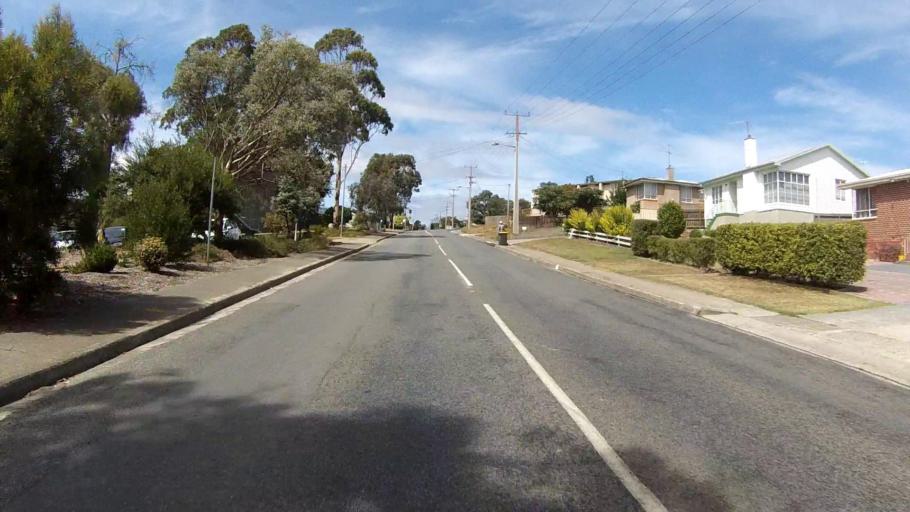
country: AU
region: Tasmania
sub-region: Clarence
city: Lindisfarne
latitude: -42.8110
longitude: 147.3512
